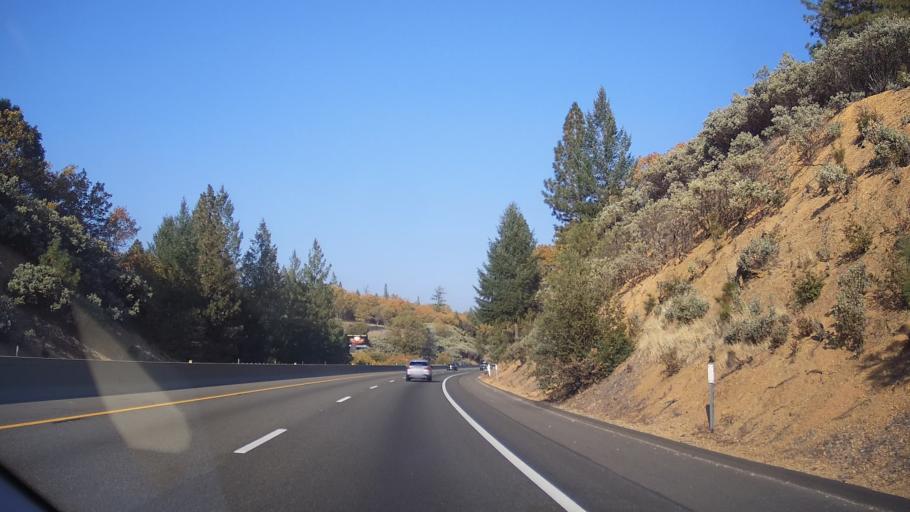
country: US
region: California
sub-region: Placer County
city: Colfax
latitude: 39.0618
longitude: -120.9679
